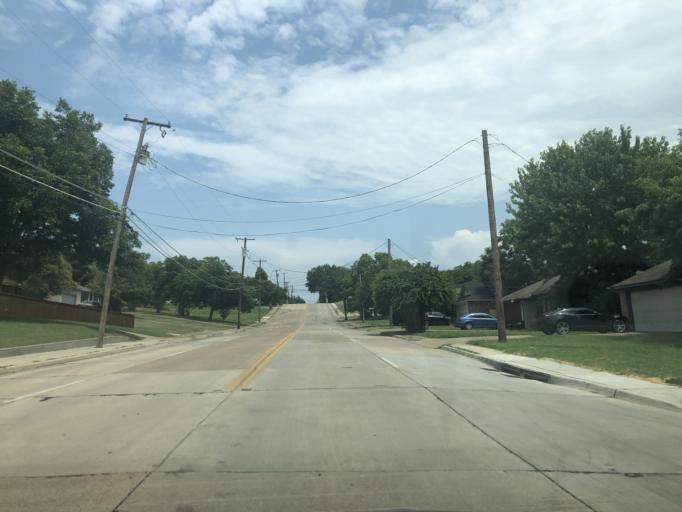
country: US
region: Texas
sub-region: Dallas County
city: Grand Prairie
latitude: 32.7488
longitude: -97.0159
